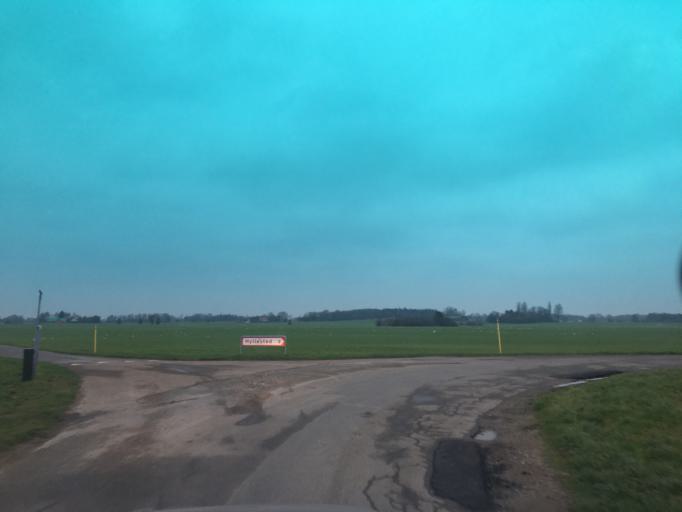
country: DK
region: Zealand
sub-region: Naestved Kommune
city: Fuglebjerg
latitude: 55.2745
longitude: 11.4264
